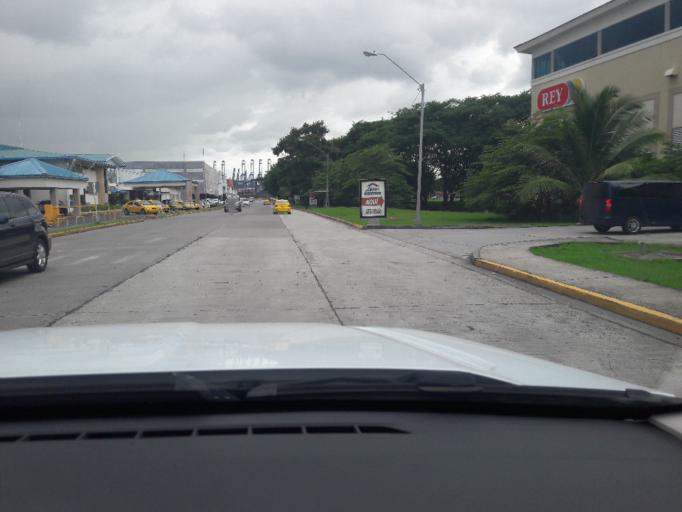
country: PA
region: Panama
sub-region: Distrito de Panama
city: Ancon
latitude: 8.9715
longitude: -79.5598
